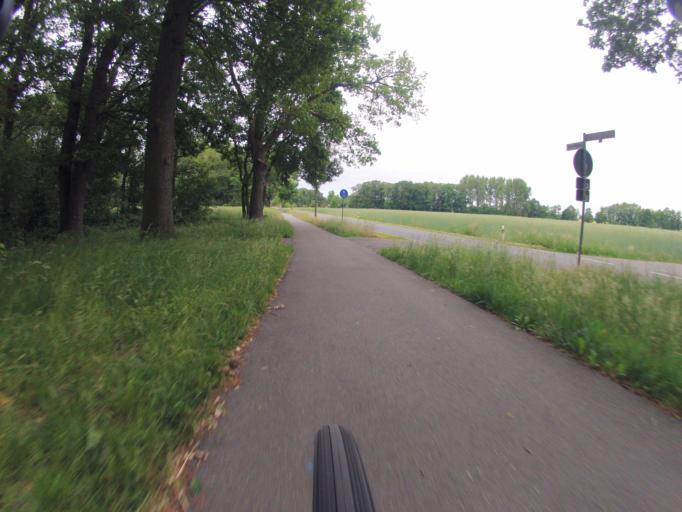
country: DE
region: North Rhine-Westphalia
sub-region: Regierungsbezirk Munster
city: Saerbeck
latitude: 52.1625
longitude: 7.6121
